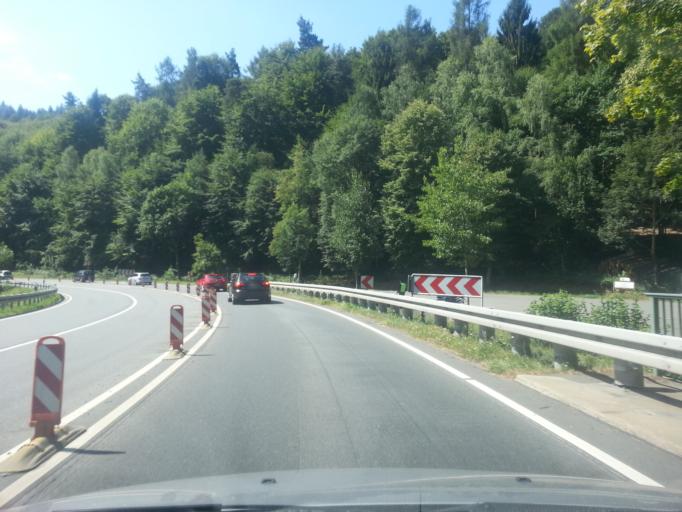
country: DE
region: Hesse
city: Hochst im Odenwald
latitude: 49.8133
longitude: 8.9705
